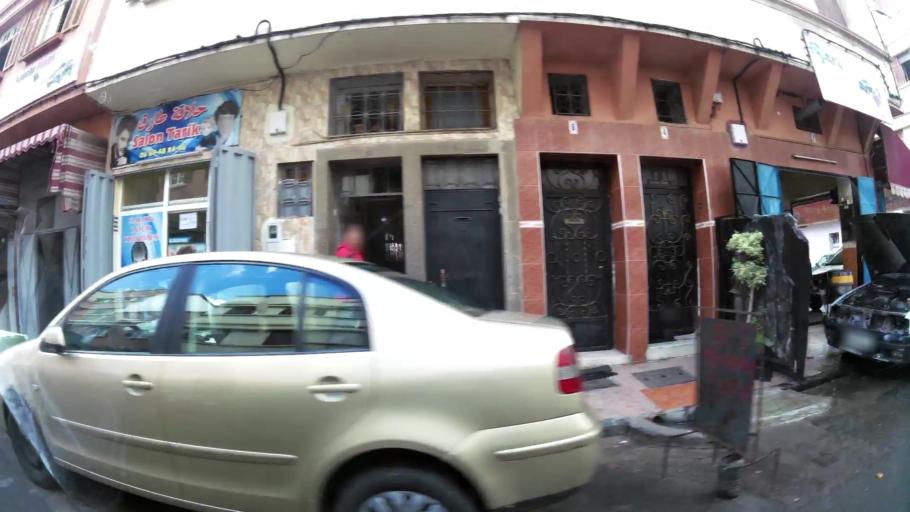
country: MA
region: Grand Casablanca
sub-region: Casablanca
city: Casablanca
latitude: 33.5613
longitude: -7.6083
